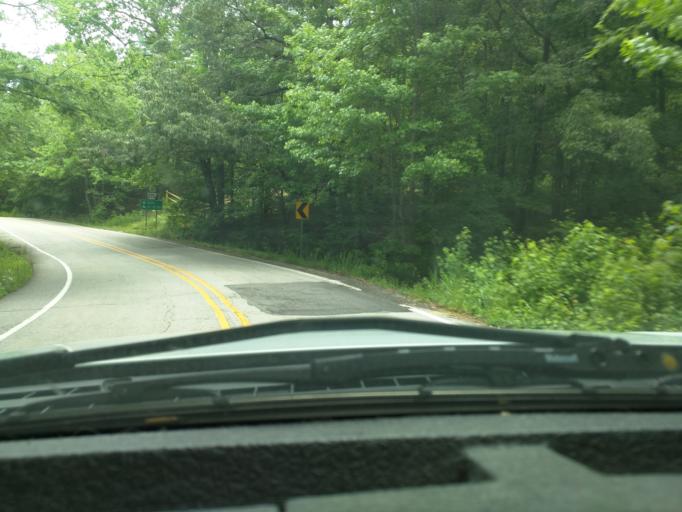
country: US
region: Arkansas
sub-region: Franklin County
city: Ozark
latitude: 35.6926
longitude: -93.8123
